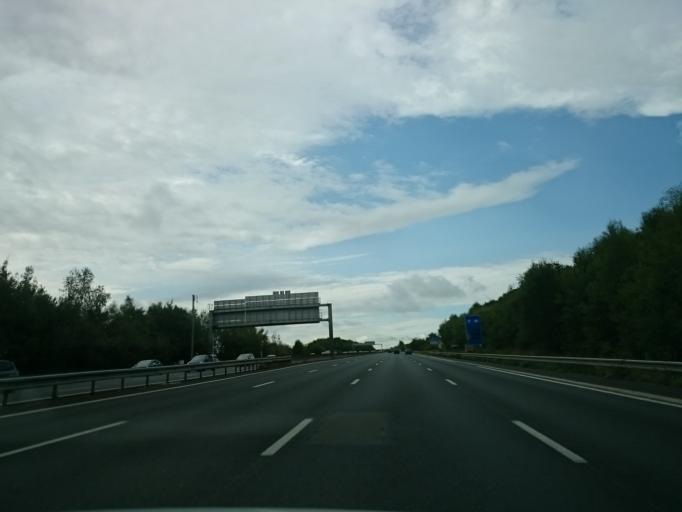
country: FR
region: Ile-de-France
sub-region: Departement de l'Essonne
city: Fontenay-les-Briis
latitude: 48.6469
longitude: 2.1645
